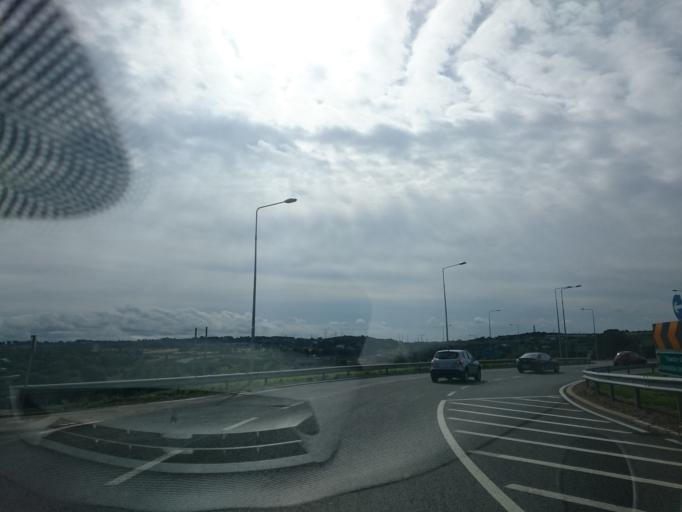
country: IE
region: Munster
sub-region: Waterford
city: Waterford
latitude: 52.2829
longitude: -7.1442
